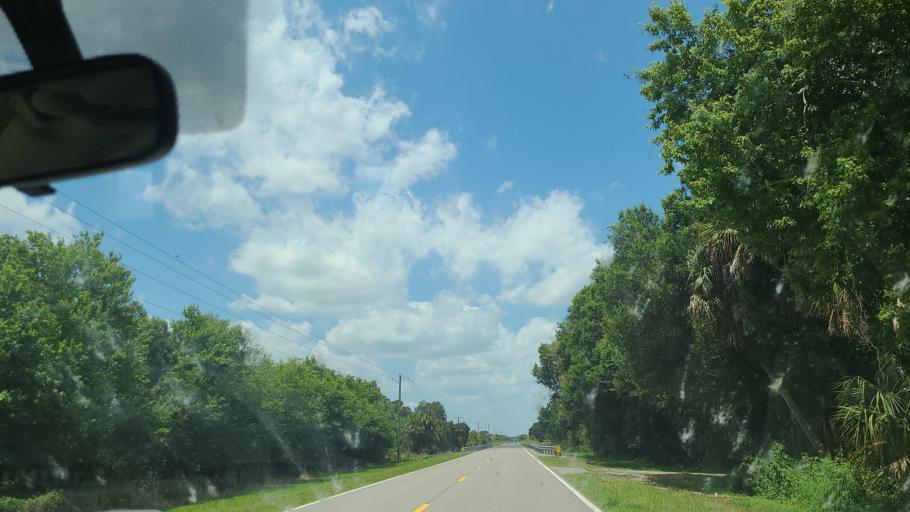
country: US
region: Florida
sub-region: Okeechobee County
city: Cypress Quarters
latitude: 27.3945
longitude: -80.8933
